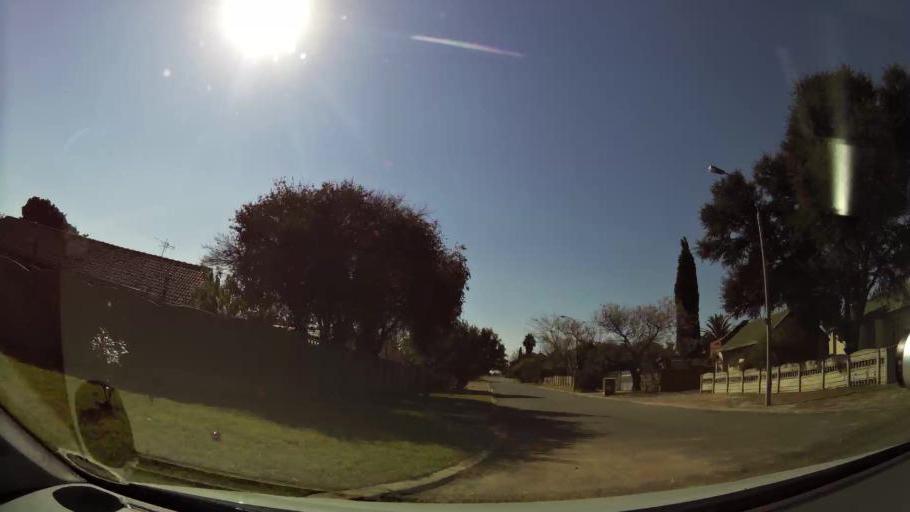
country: ZA
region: Gauteng
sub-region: Ekurhuleni Metropolitan Municipality
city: Tembisa
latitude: -26.0510
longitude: 28.2226
